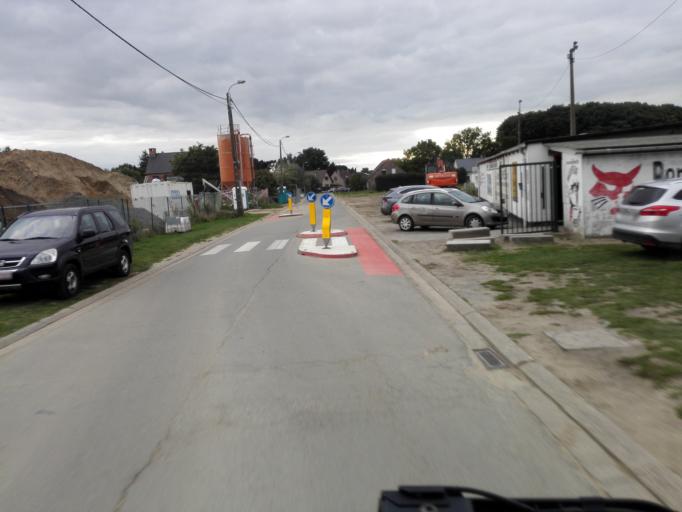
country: BE
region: Flanders
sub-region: Provincie Antwerpen
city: Bonheiden
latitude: 50.9941
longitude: 4.5436
